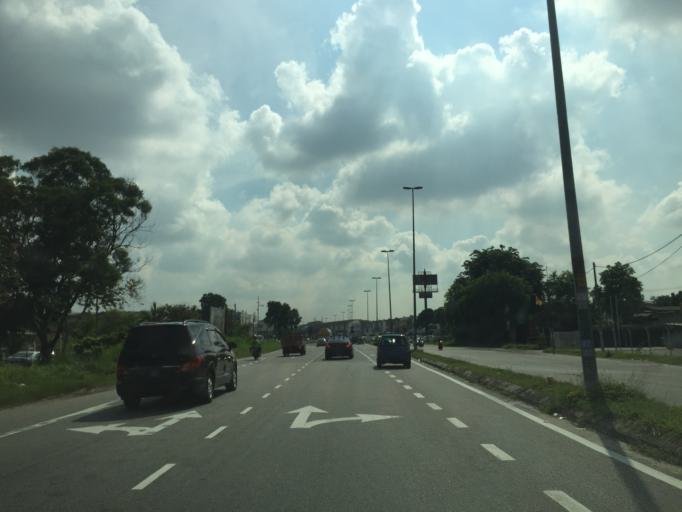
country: MY
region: Selangor
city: Klang
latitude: 3.0118
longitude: 101.4637
